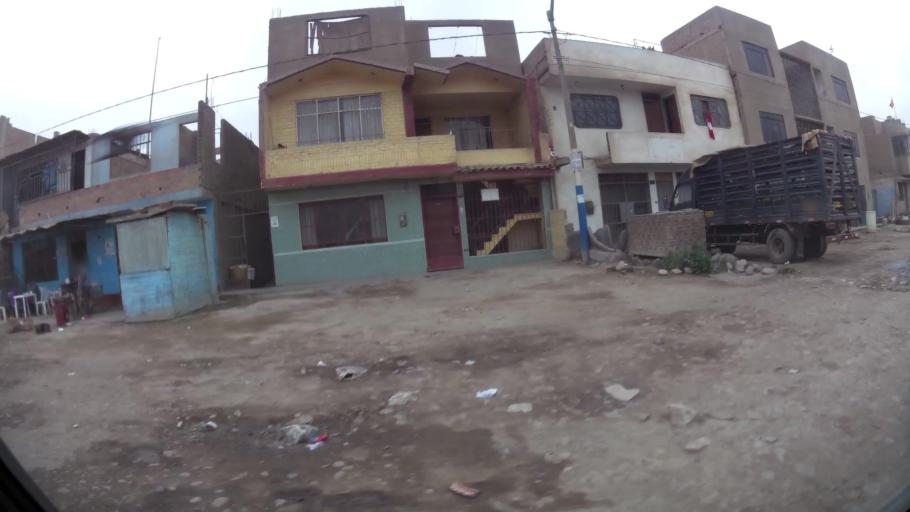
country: PE
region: Lima
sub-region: Lima
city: Independencia
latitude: -11.9558
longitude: -77.0994
